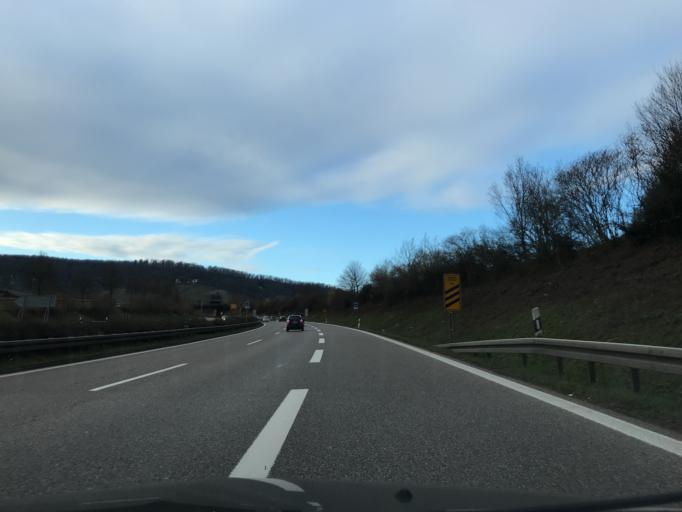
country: DE
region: Baden-Wuerttemberg
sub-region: Regierungsbezirk Stuttgart
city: Fellbach
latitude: 48.8123
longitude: 9.2924
